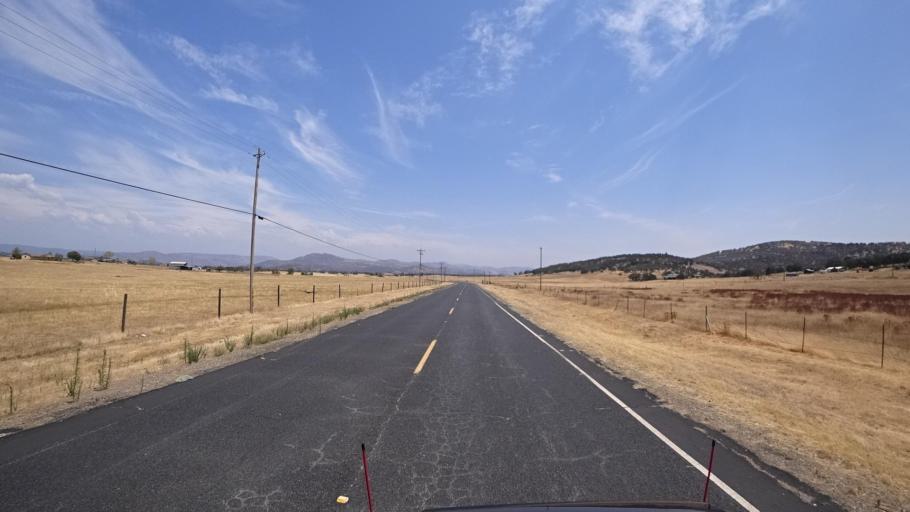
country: US
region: California
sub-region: Tuolumne County
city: Jamestown
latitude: 37.6462
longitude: -120.3229
